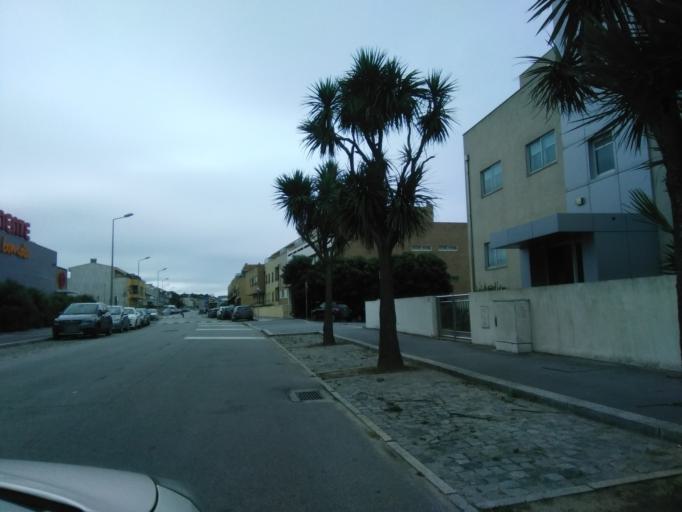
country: PT
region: Porto
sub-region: Matosinhos
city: Lavra
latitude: 41.2549
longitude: -8.7215
